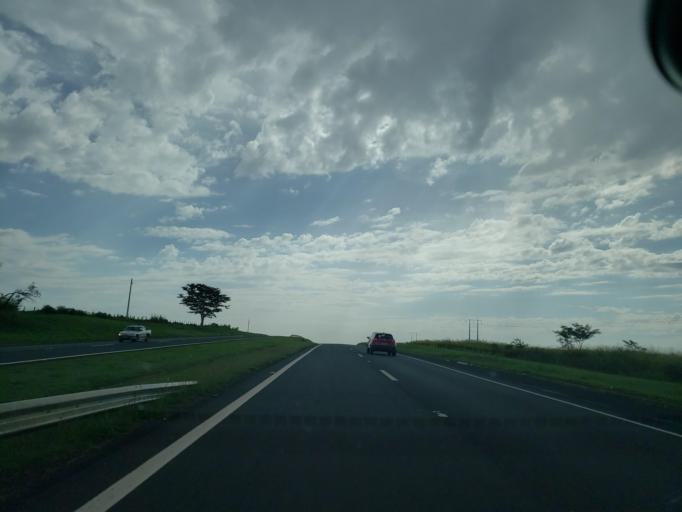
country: BR
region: Sao Paulo
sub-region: Cafelandia
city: Cafelandia
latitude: -21.7515
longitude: -49.6848
